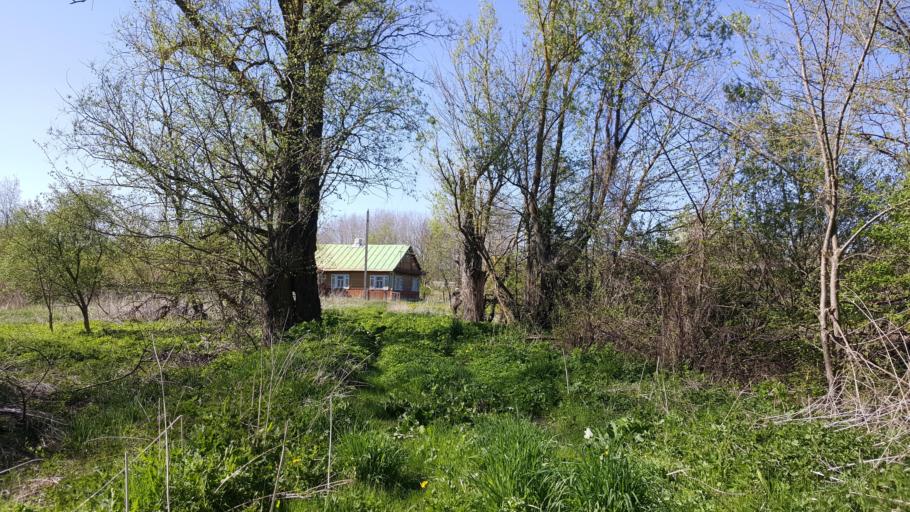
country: BY
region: Brest
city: Kamyanyets
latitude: 52.4346
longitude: 23.8732
